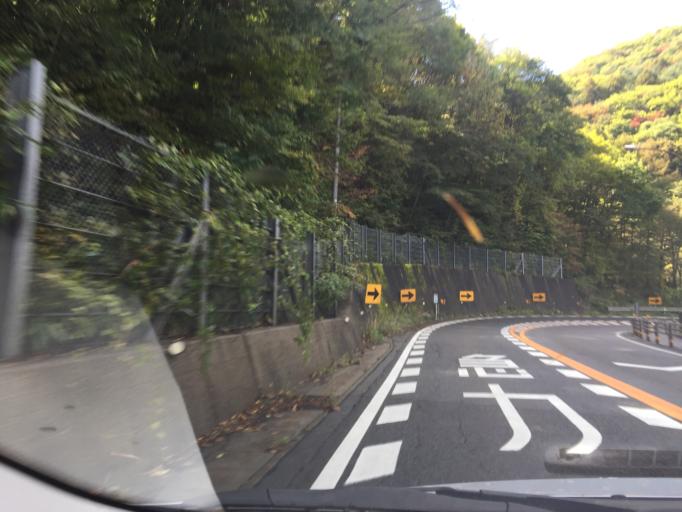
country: JP
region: Gifu
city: Nakatsugawa
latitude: 35.3613
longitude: 137.6711
